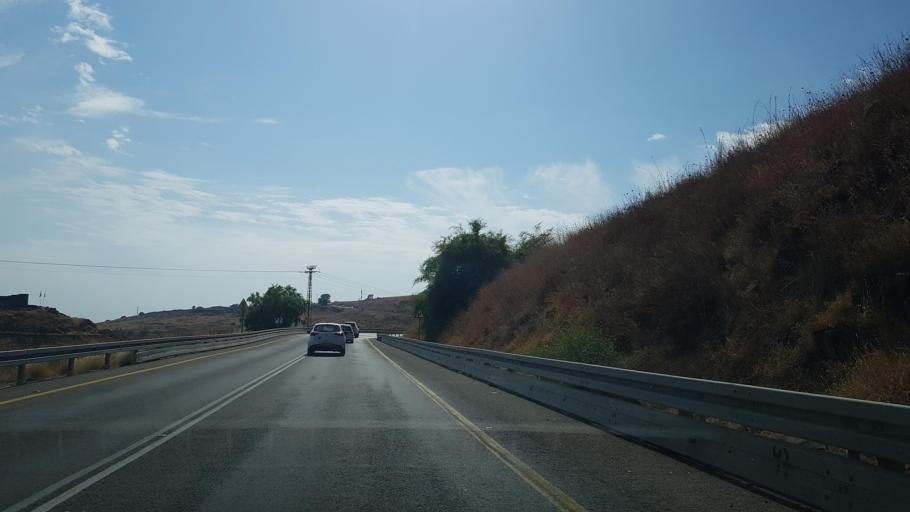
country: IL
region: Northern District
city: Rosh Pinna
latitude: 32.9139
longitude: 35.5630
